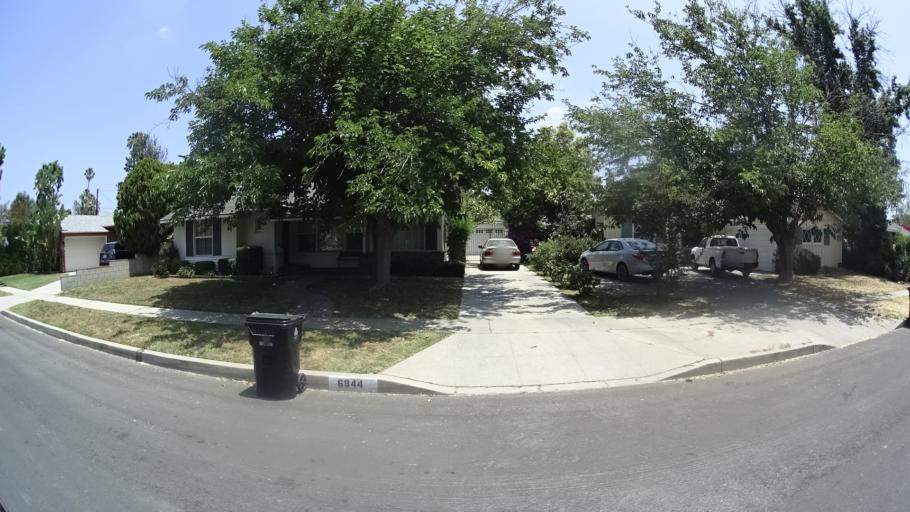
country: US
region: California
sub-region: Los Angeles County
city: Van Nuys
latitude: 34.1971
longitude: -118.4627
